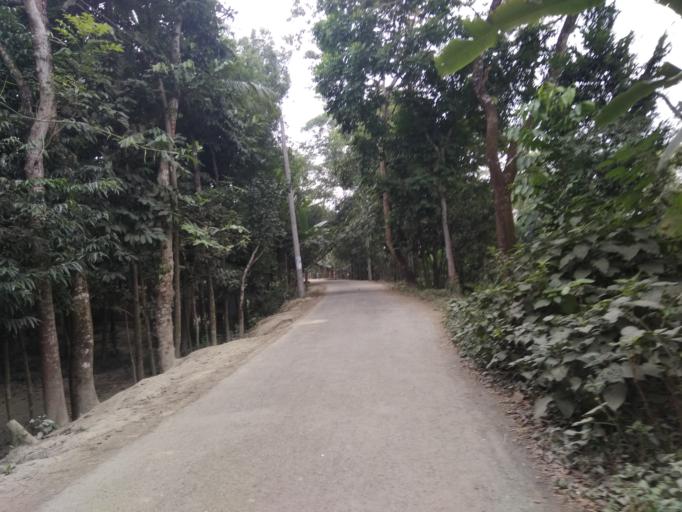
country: BD
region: Barisal
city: Mehendiganj
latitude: 22.9203
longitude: 90.3912
